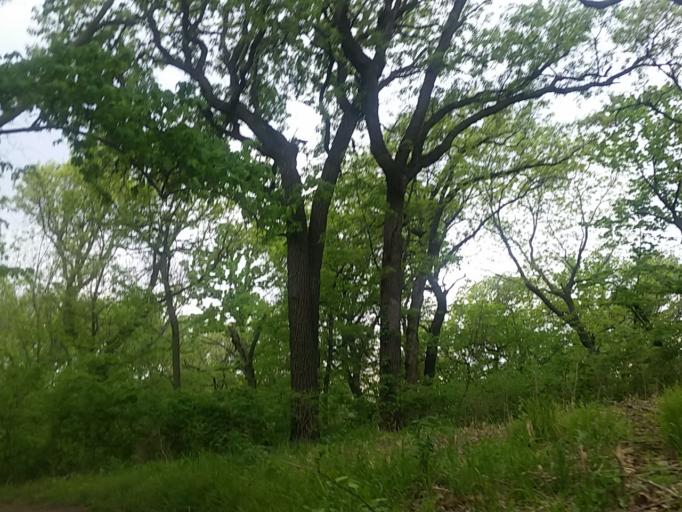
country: US
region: Nebraska
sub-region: Sarpy County
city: Bellevue
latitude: 41.1818
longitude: -95.9077
